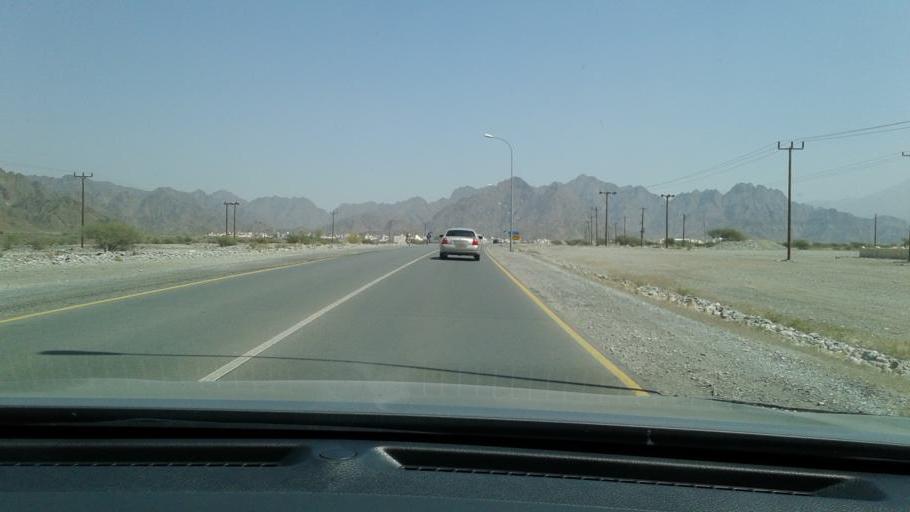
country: OM
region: Al Batinah
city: Rustaq
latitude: 23.3674
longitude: 57.4660
